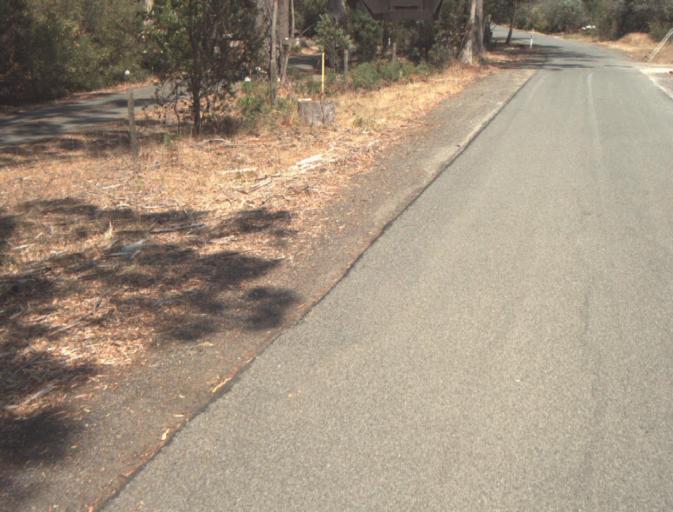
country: AU
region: Tasmania
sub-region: Launceston
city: Newstead
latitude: -41.4891
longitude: 147.1951
